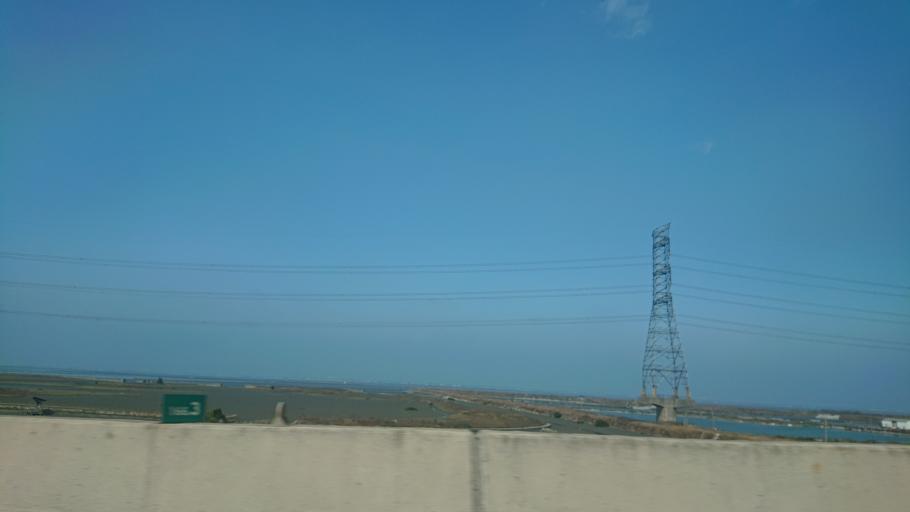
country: TW
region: Taiwan
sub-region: Changhua
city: Chang-hua
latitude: 24.1650
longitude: 120.4672
